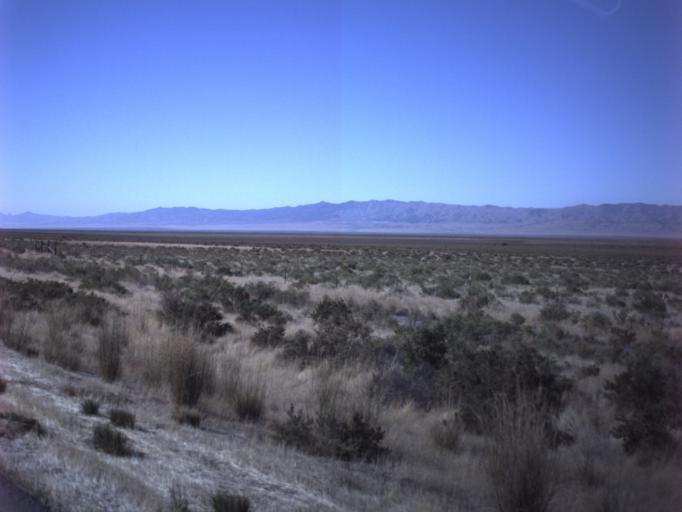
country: US
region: Utah
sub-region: Tooele County
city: Grantsville
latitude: 40.6558
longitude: -112.6816
